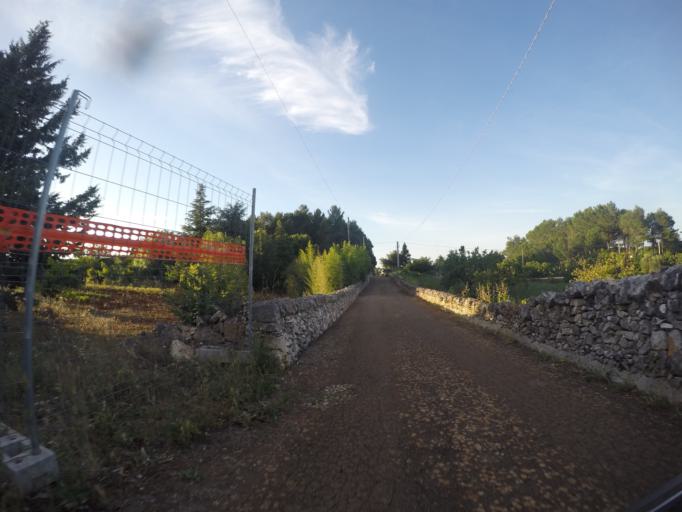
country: IT
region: Apulia
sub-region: Provincia di Taranto
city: Martina Franca
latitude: 40.6490
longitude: 17.3624
